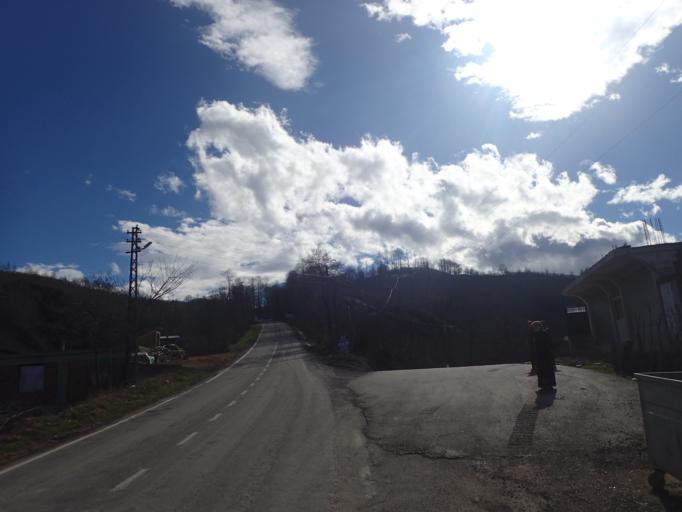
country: TR
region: Ordu
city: Camas
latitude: 40.8942
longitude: 37.5269
